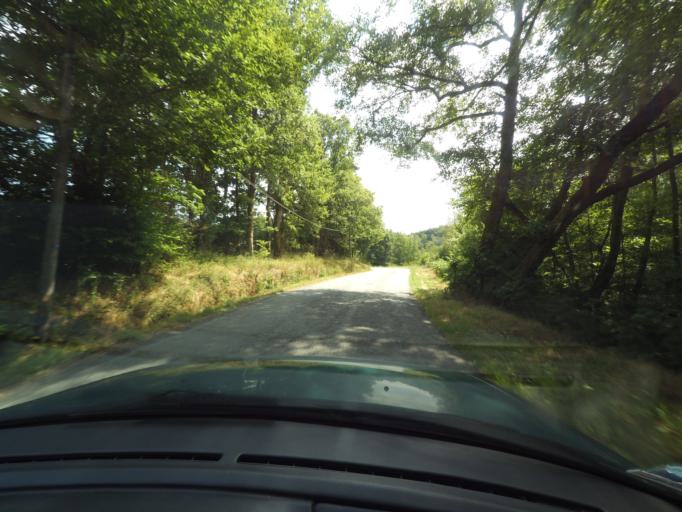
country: FR
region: Limousin
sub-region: Departement de la Correze
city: Bugeat
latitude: 45.7441
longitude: 1.9630
